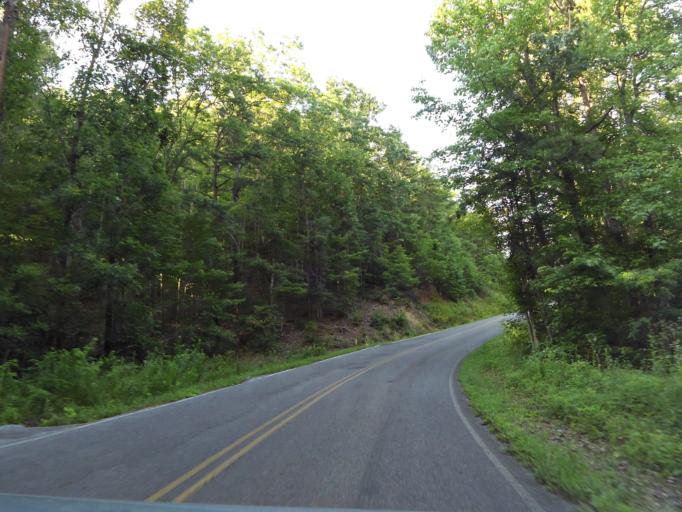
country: US
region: Tennessee
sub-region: Blount County
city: Maryville
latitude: 35.6247
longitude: -83.9398
